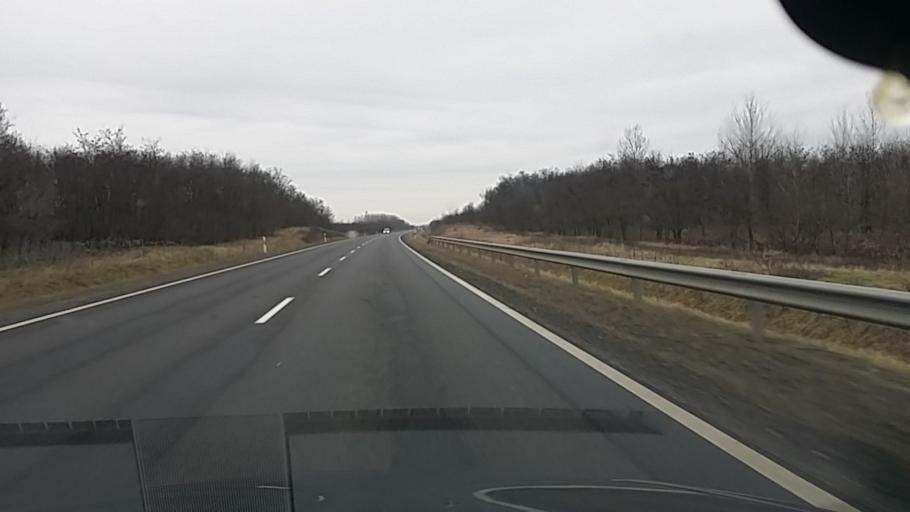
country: HU
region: Szabolcs-Szatmar-Bereg
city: Napkor
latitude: 47.9238
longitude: 21.8199
